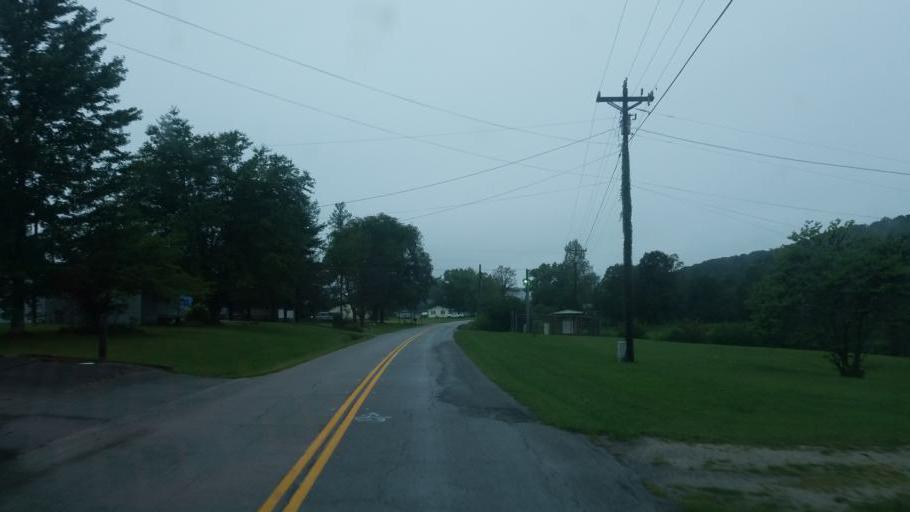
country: US
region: Kentucky
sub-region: Fleming County
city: Flemingsburg
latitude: 38.4032
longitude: -83.6277
